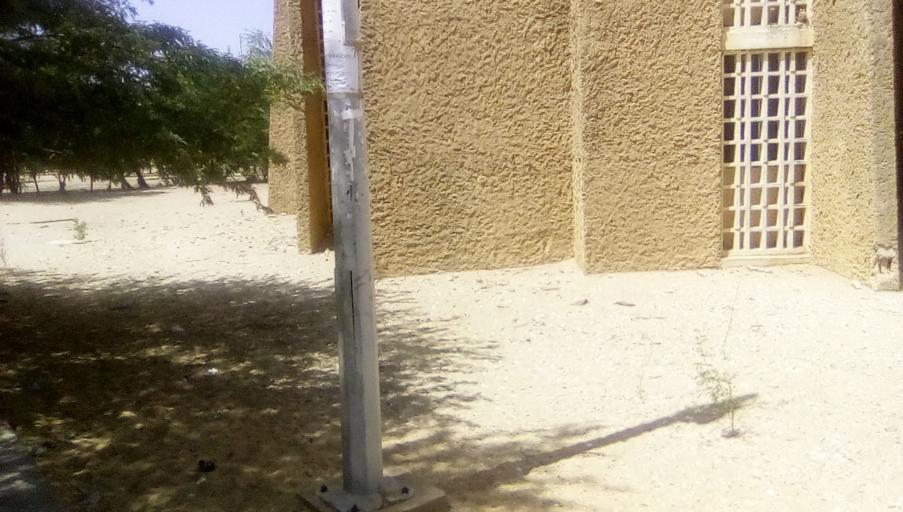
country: SN
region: Saint-Louis
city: Saint-Louis
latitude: 16.0647
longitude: -16.4219
